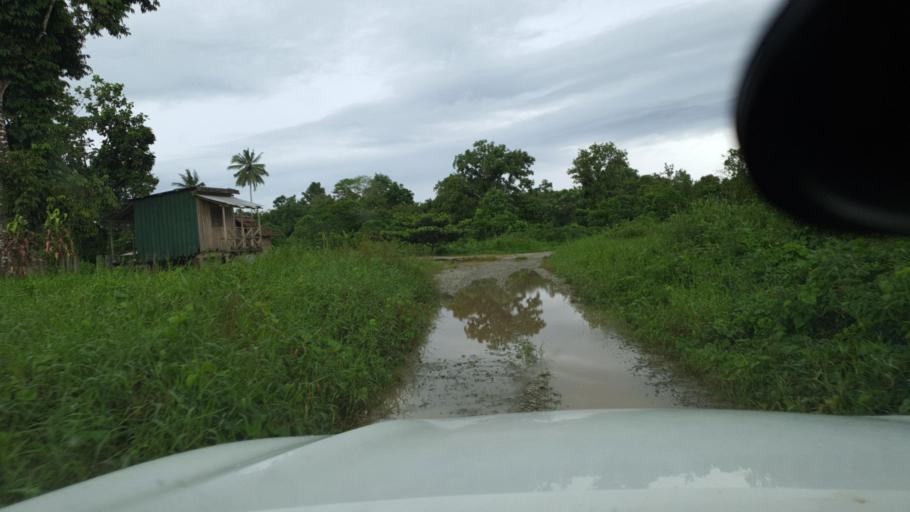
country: SB
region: Guadalcanal
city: Honiara
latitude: -9.4643
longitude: 160.3635
